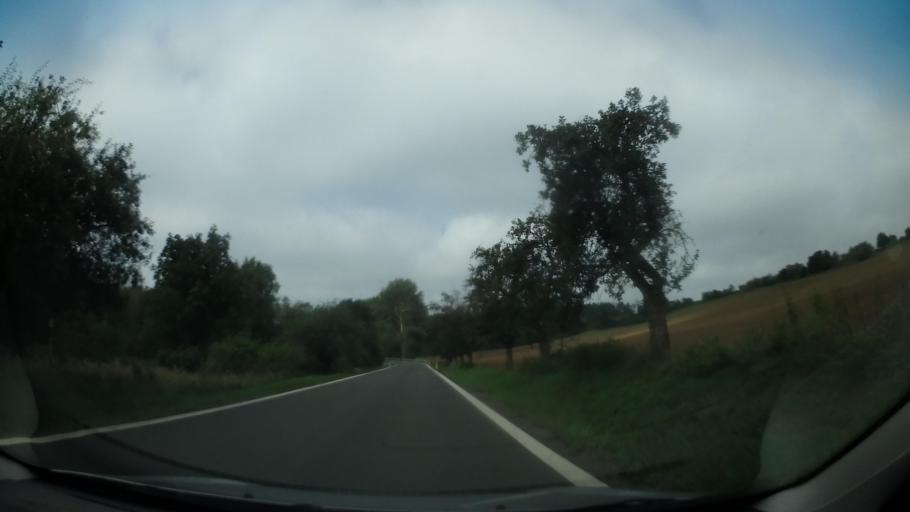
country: CZ
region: Central Bohemia
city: Neveklov
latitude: 49.7538
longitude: 14.5776
